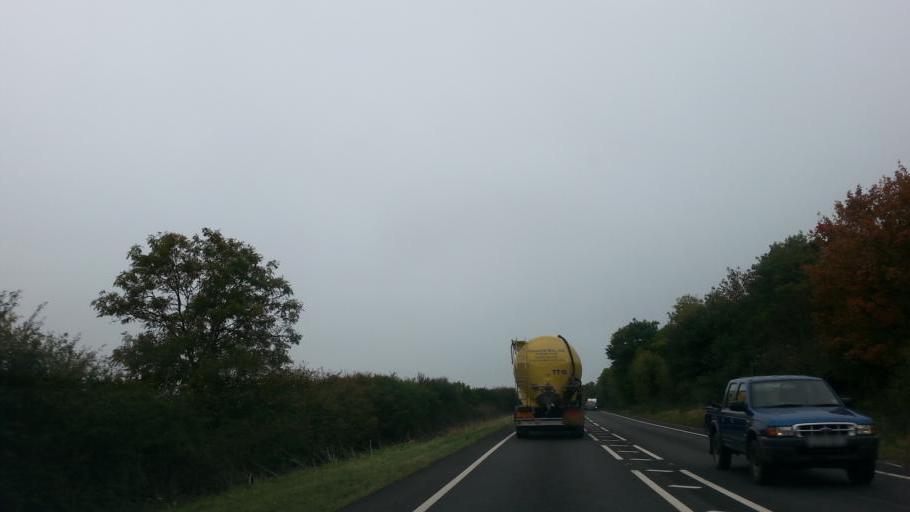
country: GB
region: England
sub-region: Northamptonshire
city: Oundle
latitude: 52.4476
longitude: -0.4654
